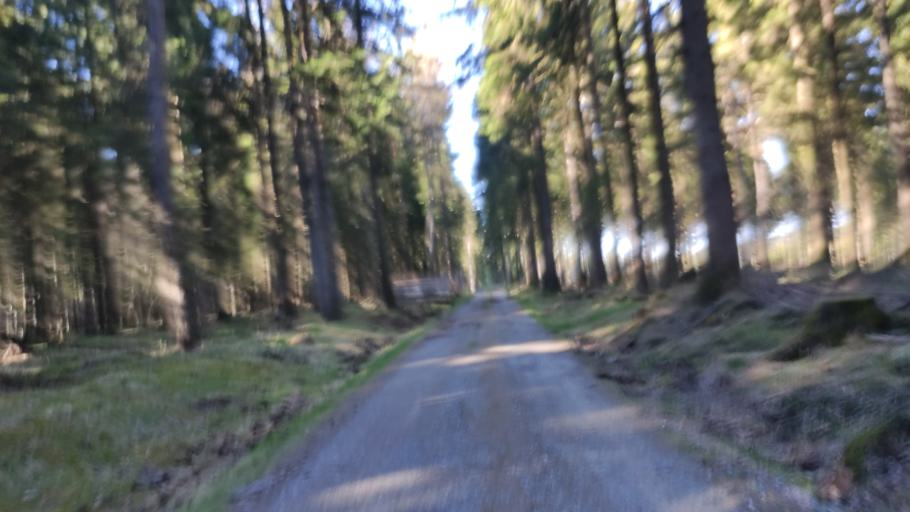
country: DE
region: Bavaria
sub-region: Upper Franconia
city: Reichenbach
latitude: 50.4424
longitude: 11.4322
